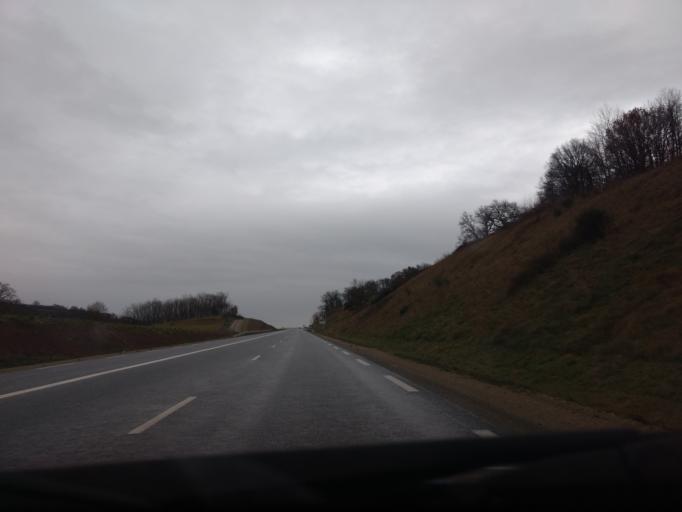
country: FR
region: Midi-Pyrenees
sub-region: Departement de l'Aveyron
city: Firmi
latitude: 44.5166
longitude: 2.3476
